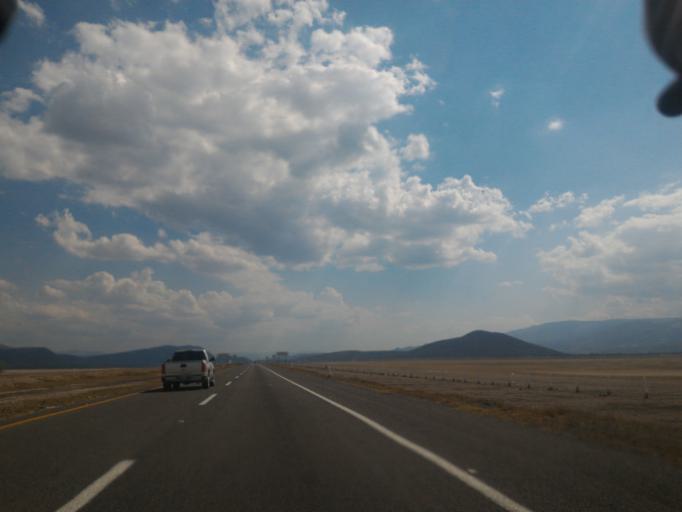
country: MX
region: Jalisco
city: Zacoalco de Torres
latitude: 20.3055
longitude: -103.5605
